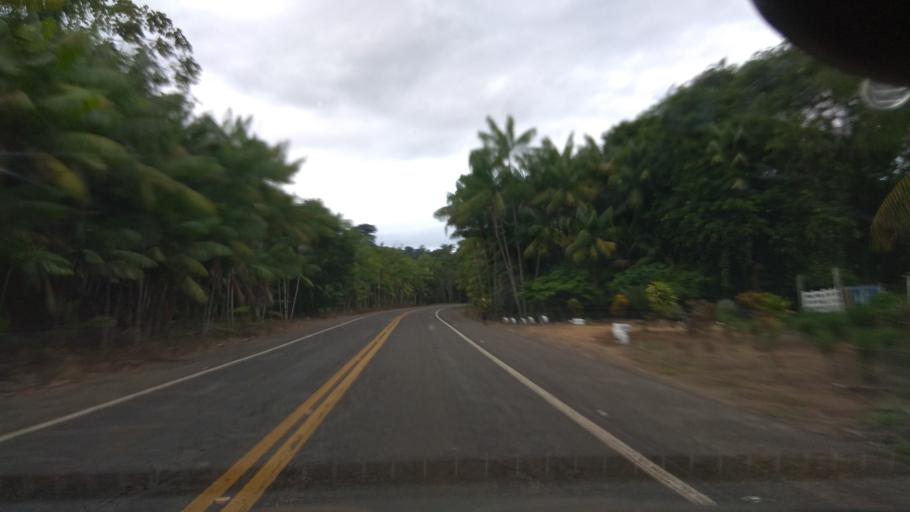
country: BR
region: Bahia
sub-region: Ubata
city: Ubata
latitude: -14.2292
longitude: -39.4396
